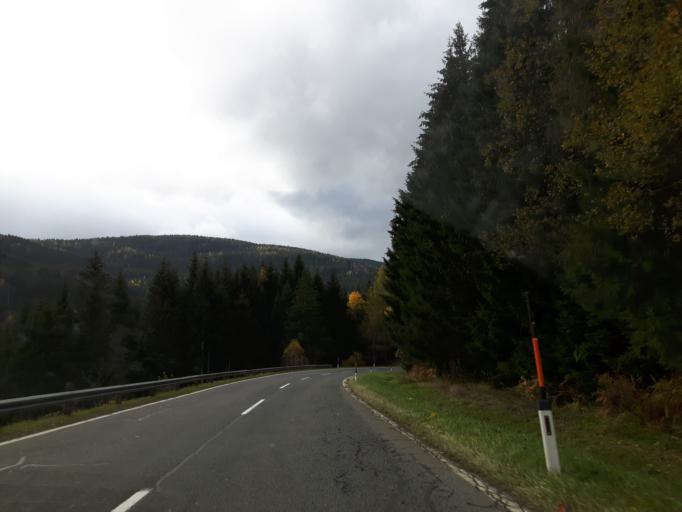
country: AT
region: Styria
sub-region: Politischer Bezirk Deutschlandsberg
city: Soboth
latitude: 46.7067
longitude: 15.1007
